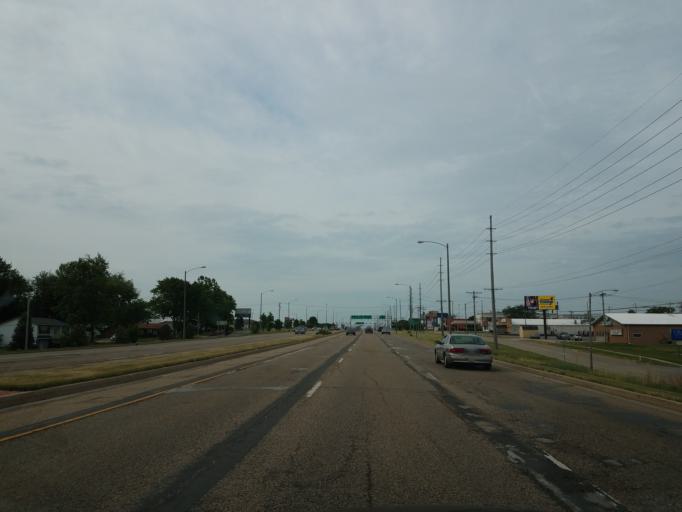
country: US
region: Illinois
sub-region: McLean County
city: Bloomington
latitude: 40.4938
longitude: -88.9531
